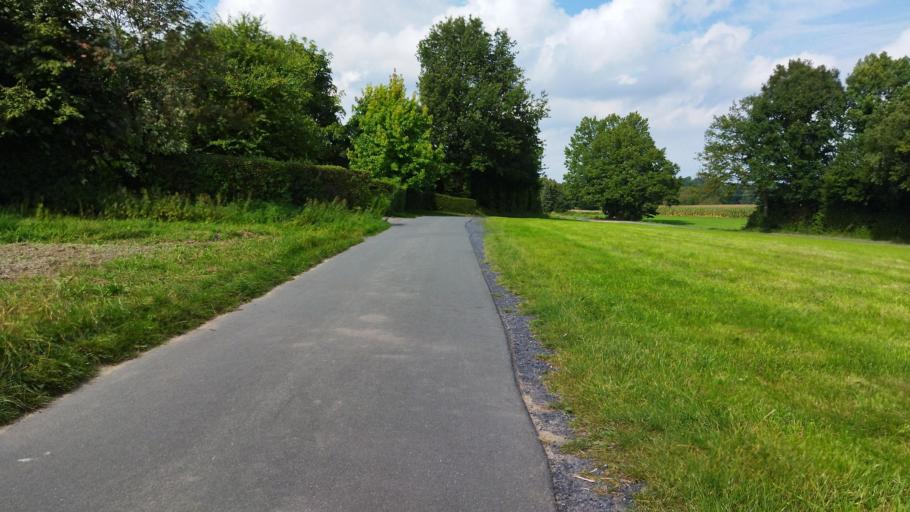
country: DE
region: North Rhine-Westphalia
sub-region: Regierungsbezirk Munster
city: Telgte
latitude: 51.9781
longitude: 7.8039
